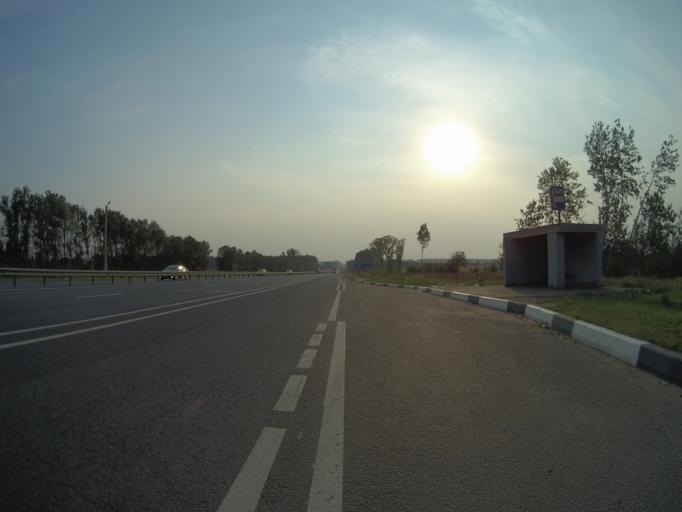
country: RU
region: Vladimir
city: Novki
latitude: 56.2031
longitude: 41.1296
